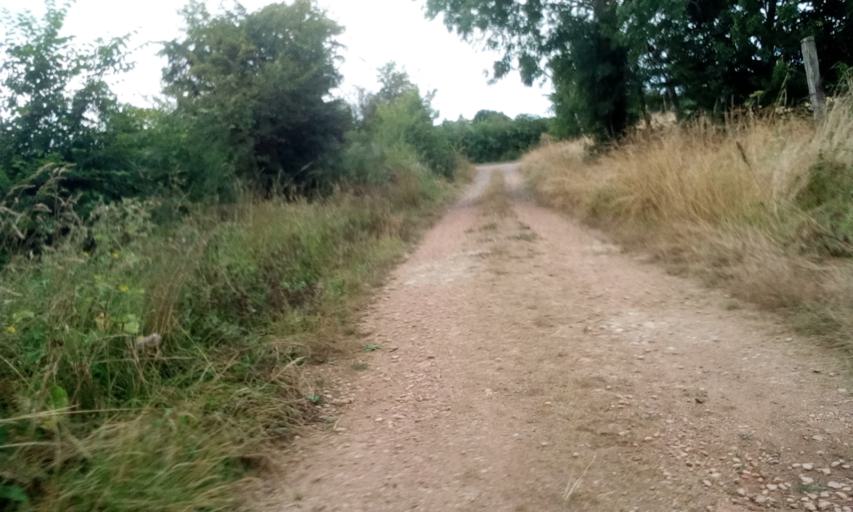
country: FR
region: Lower Normandy
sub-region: Departement du Calvados
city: Sannerville
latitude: 49.1909
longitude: -0.2193
